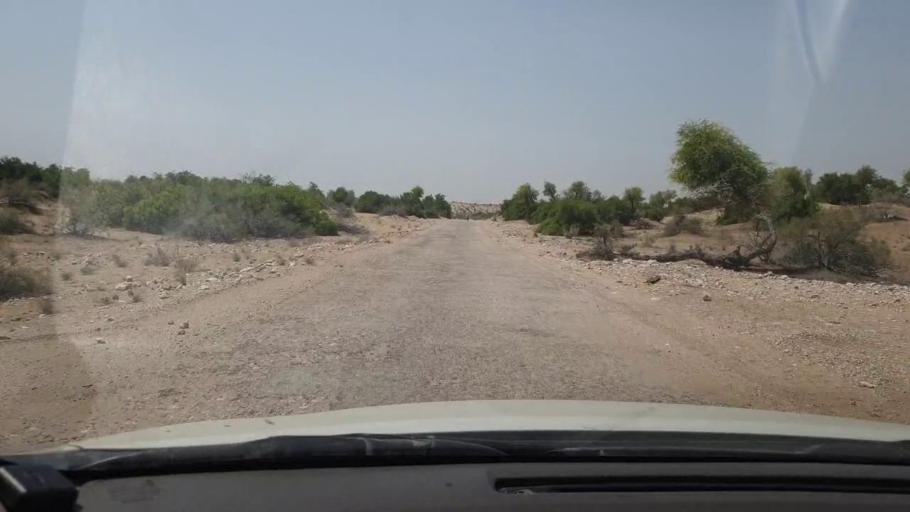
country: PK
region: Sindh
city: Rohri
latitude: 27.3120
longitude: 69.2817
